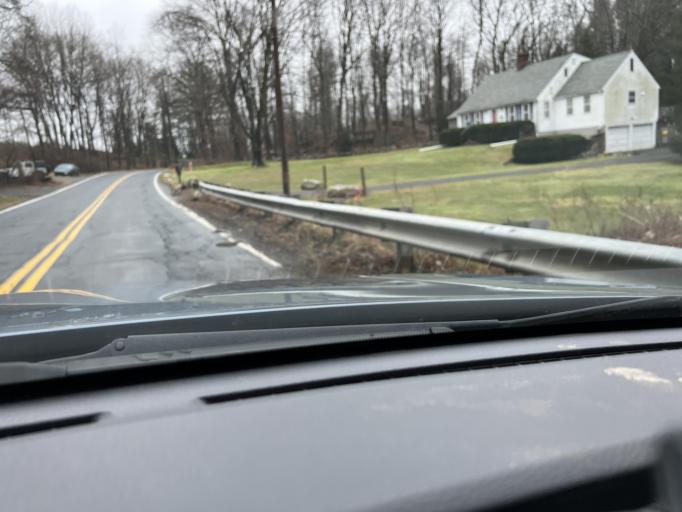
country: US
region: Massachusetts
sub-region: Hampden County
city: Southwick
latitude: 42.0380
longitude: -72.7152
